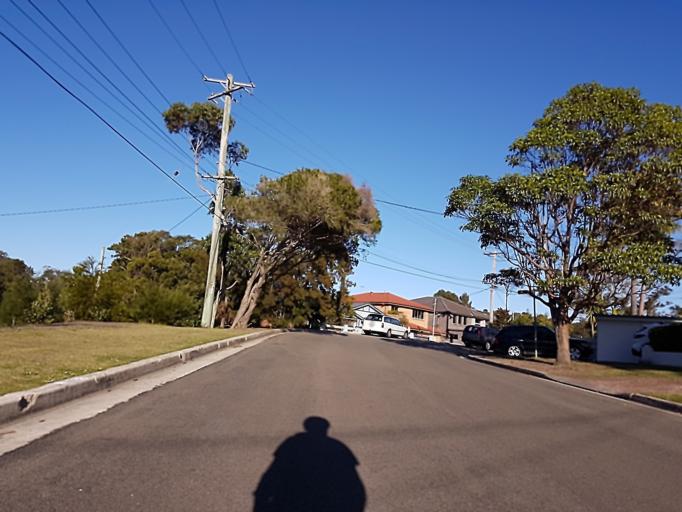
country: AU
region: New South Wales
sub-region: Manly Vale
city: Balgowlah
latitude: -33.7915
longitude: 151.2543
